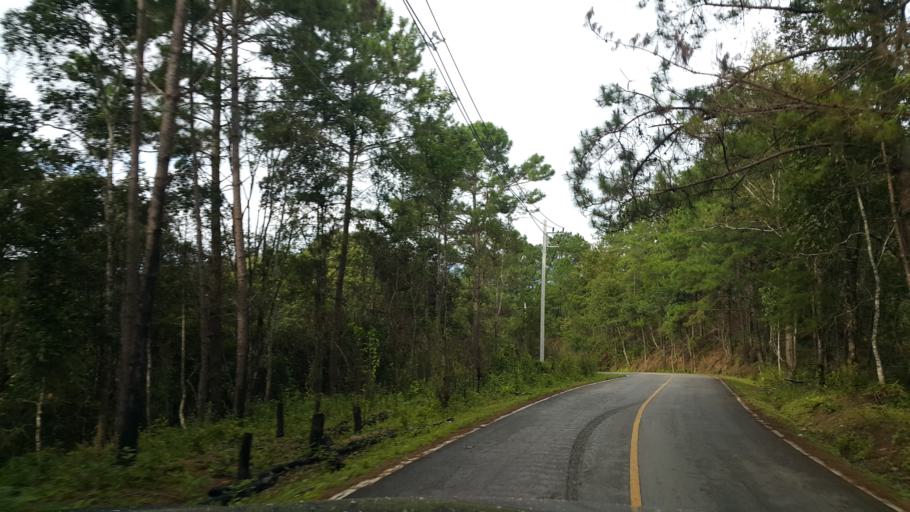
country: TH
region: Chiang Mai
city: Samoeng
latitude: 18.8979
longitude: 98.4998
